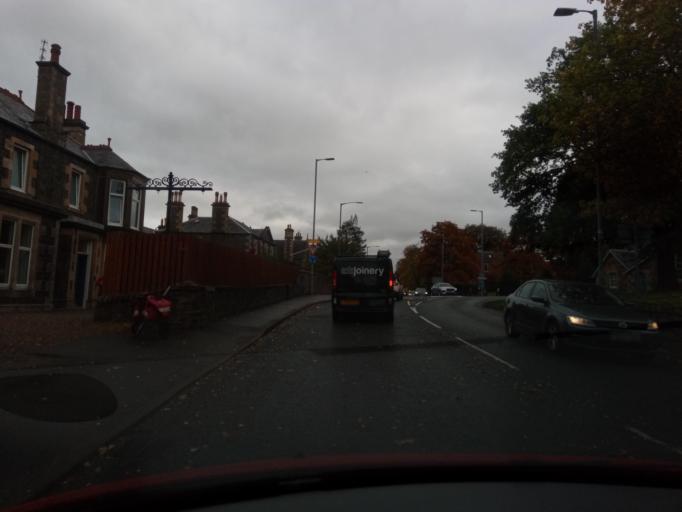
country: GB
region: Scotland
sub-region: The Scottish Borders
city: Galashiels
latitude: 55.6121
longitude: -2.8029
